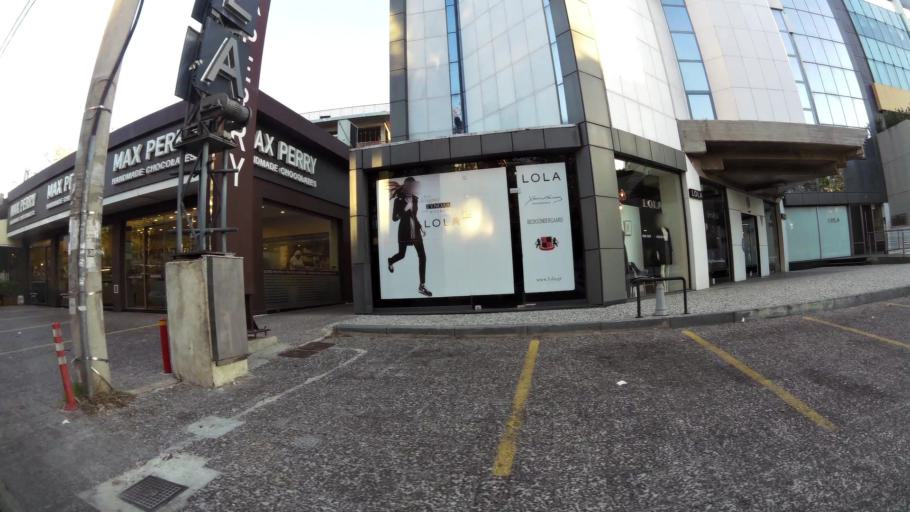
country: GR
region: Attica
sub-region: Nomarchia Athinas
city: Marousi
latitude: 38.0477
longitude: 23.8044
